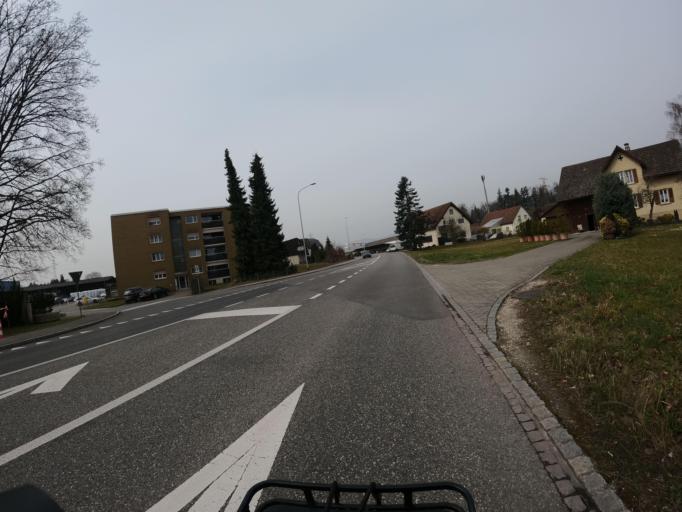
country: CH
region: Aargau
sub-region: Bezirk Brugg
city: Rupperswil
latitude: 47.4044
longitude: 8.1223
